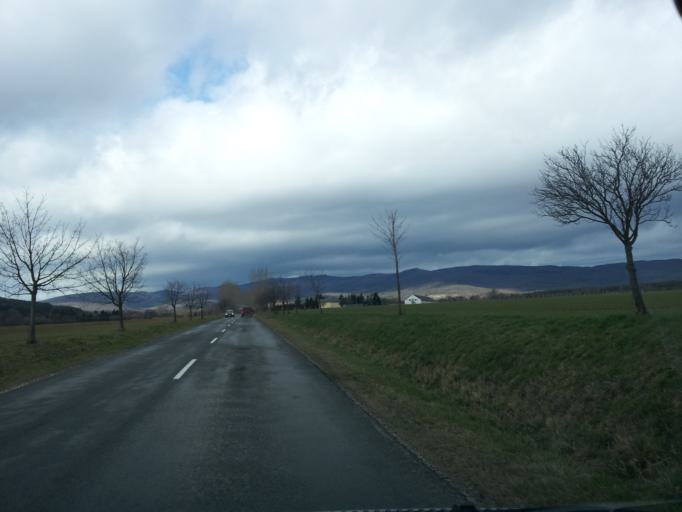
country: HU
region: Vas
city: Koszeg
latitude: 47.3441
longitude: 16.5556
